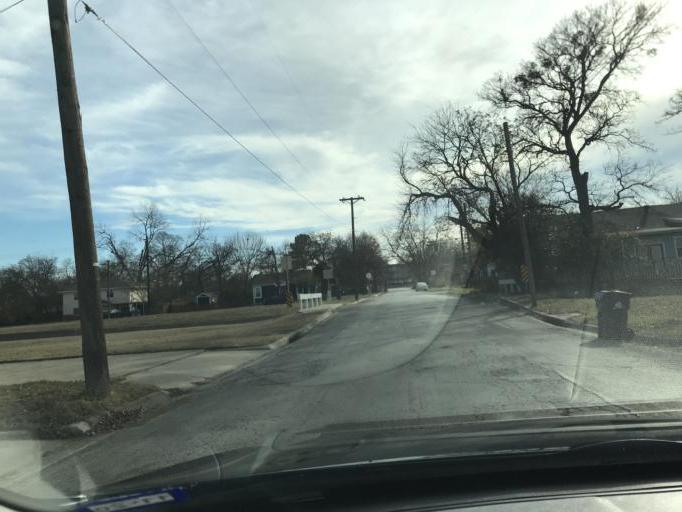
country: US
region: Texas
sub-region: Denton County
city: Denton
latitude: 33.2221
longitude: -97.1402
